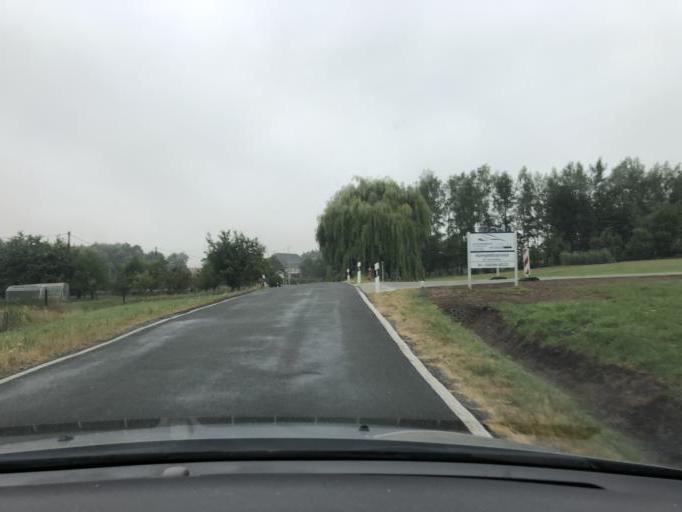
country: DE
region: Saxony
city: Narsdorf
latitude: 50.9929
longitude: 12.6830
